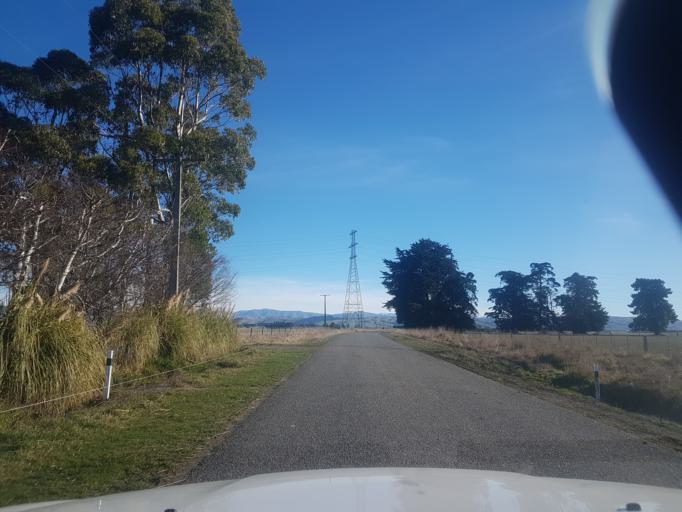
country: NZ
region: Canterbury
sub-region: Timaru District
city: Pleasant Point
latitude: -44.2541
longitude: 171.0395
